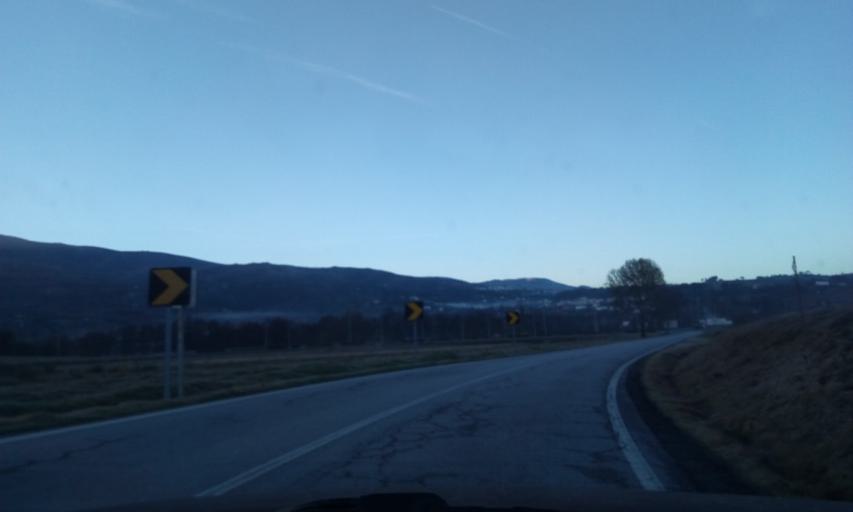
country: PT
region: Guarda
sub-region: Fornos de Algodres
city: Fornos de Algodres
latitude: 40.5369
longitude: -7.5702
